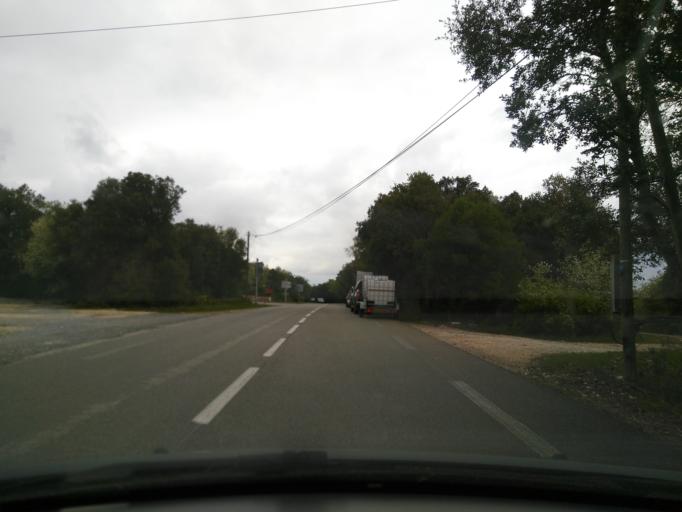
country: FR
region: Languedoc-Roussillon
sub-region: Departement du Gard
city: Barjac
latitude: 44.3271
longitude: 4.4166
